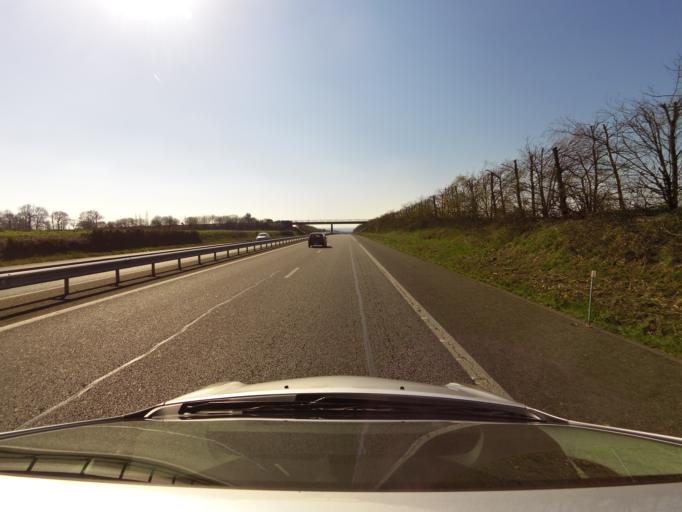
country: FR
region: Brittany
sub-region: Departement d'Ille-et-Vilaine
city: Plelan-le-Grand
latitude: 47.9710
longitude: -2.0965
